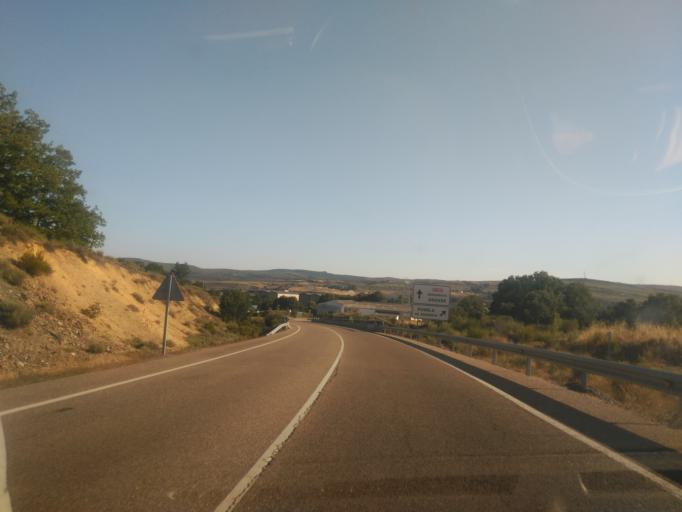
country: ES
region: Castille and Leon
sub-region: Provincia de Zamora
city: Puebla de Sanabria
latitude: 42.0641
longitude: -6.6223
